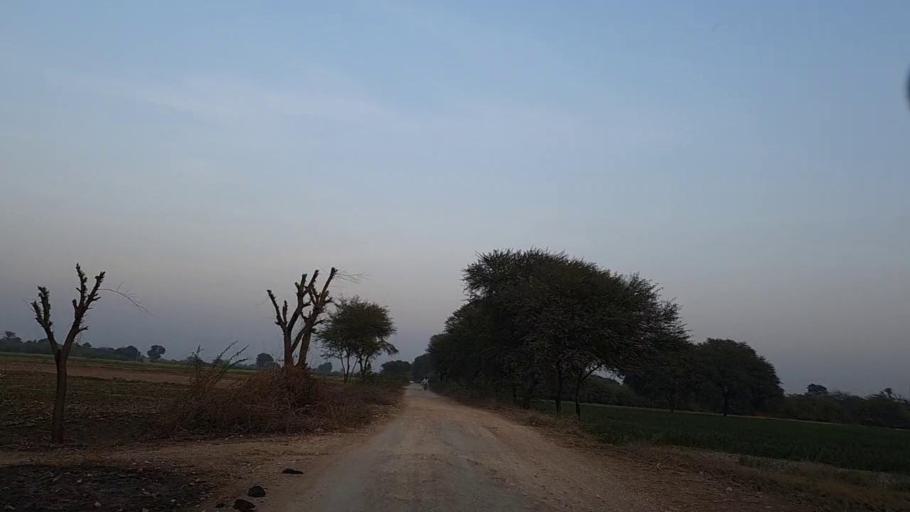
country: PK
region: Sindh
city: Tando Ghulam Ali
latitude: 25.1514
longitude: 68.9377
